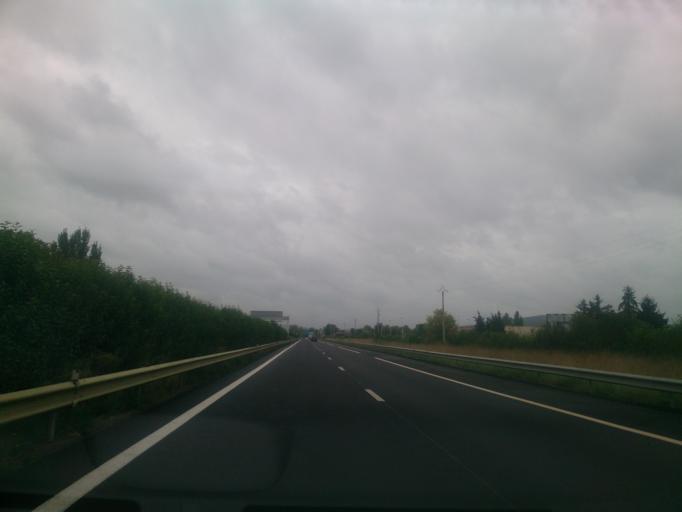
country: FR
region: Midi-Pyrenees
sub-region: Departement de la Haute-Garonne
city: Martres-Tolosane
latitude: 43.2140
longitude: 1.0359
